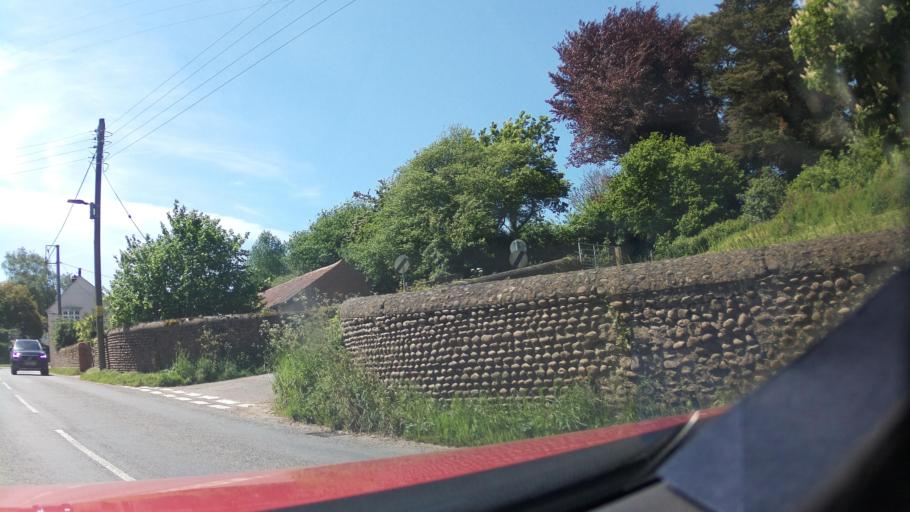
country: GB
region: England
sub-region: Devon
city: Newton Poppleford
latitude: 50.6788
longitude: -3.3074
